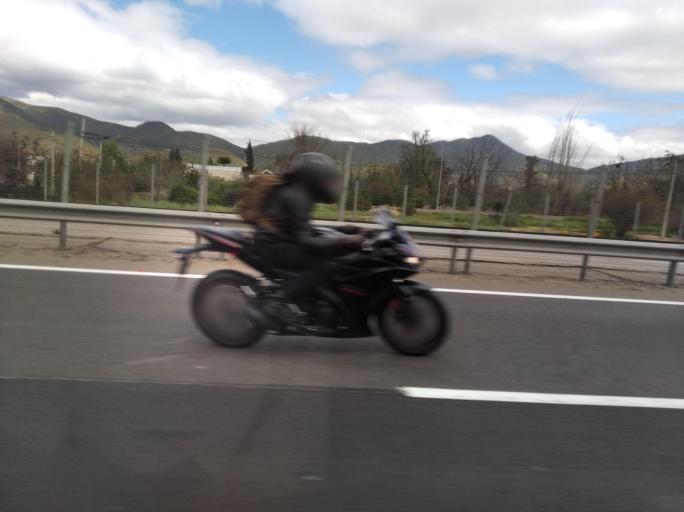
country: CL
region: Santiago Metropolitan
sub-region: Provincia de Melipilla
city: Melipilla
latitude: -33.4125
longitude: -71.1561
